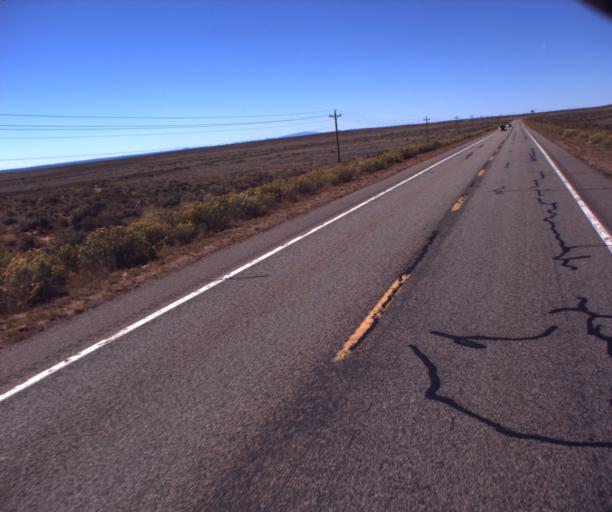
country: US
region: Arizona
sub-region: Coconino County
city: Fredonia
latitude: 36.8861
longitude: -112.6308
